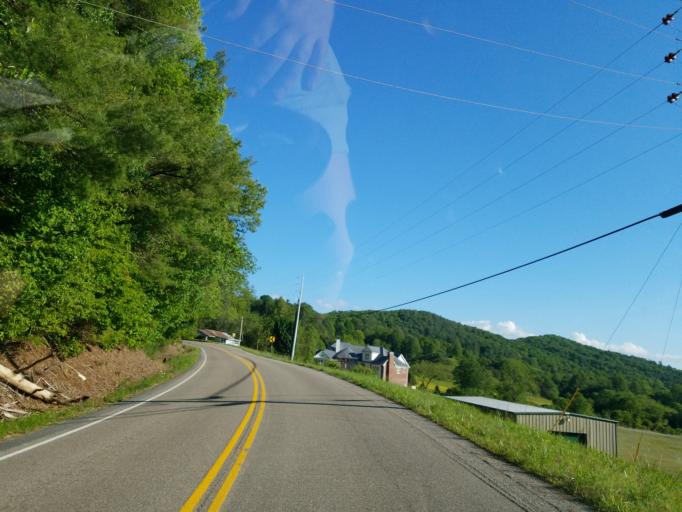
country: US
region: Georgia
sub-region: Fannin County
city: Blue Ridge
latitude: 34.7724
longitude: -84.1856
